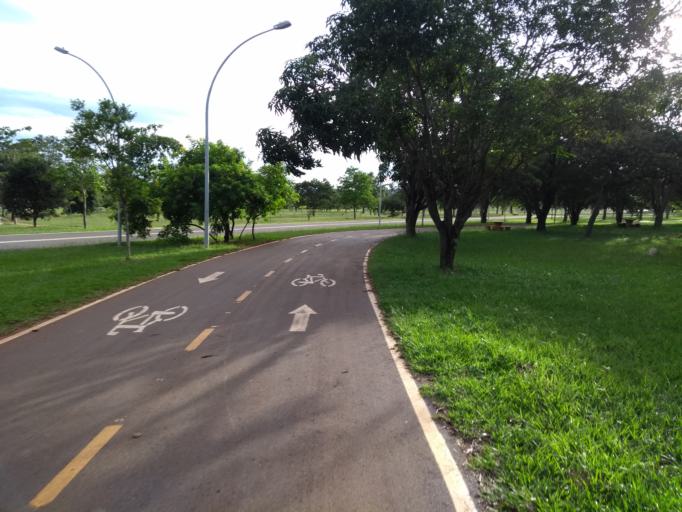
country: BR
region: Federal District
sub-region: Brasilia
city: Brasilia
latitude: -15.8092
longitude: -47.9164
